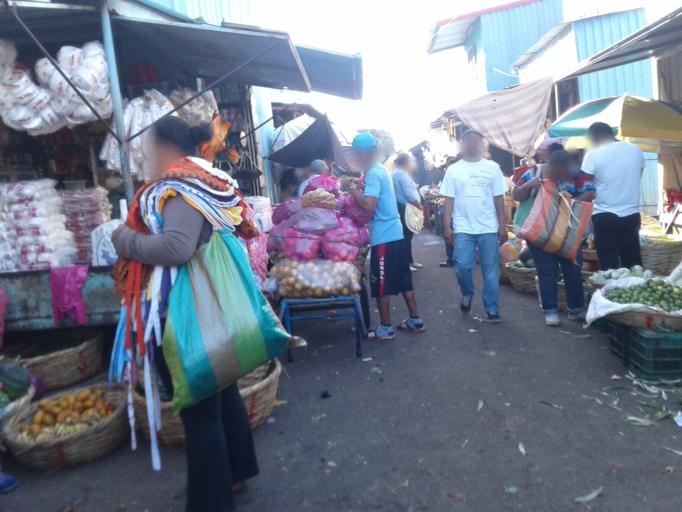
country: NI
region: Managua
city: Managua
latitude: 12.1489
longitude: -86.2642
